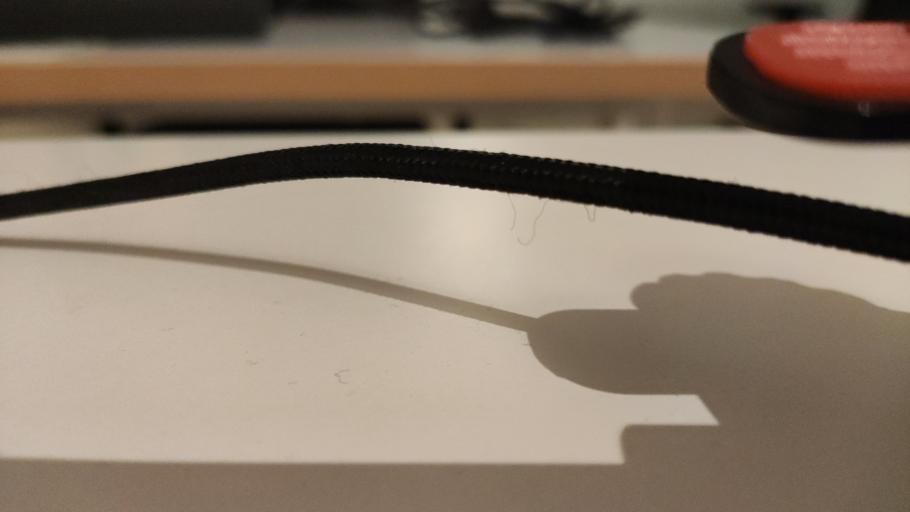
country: RU
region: Moskovskaya
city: Novoye
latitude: 55.6367
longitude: 38.9290
